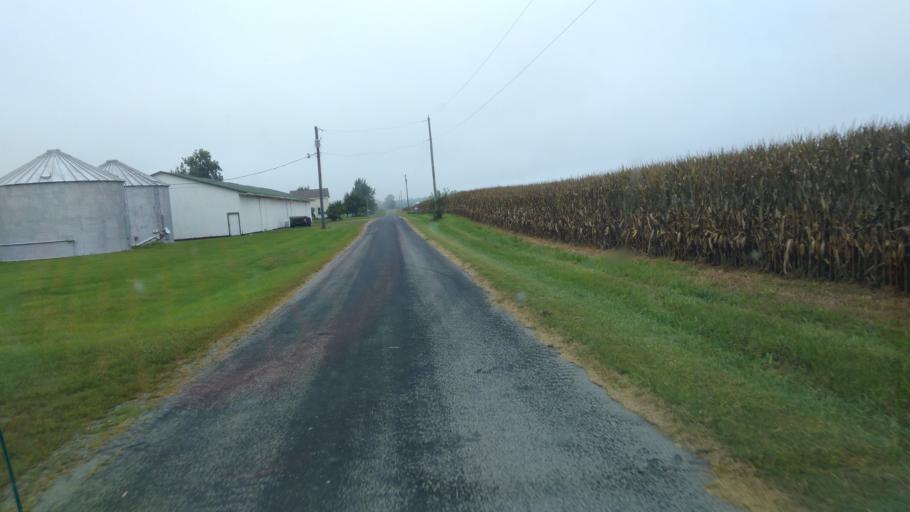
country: US
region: Ohio
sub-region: Hardin County
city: Kenton
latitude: 40.5181
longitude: -83.6004
